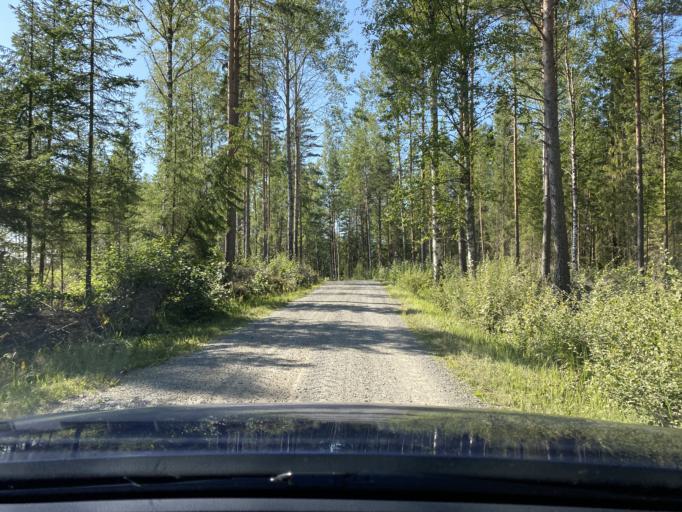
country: FI
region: Satakunta
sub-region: Rauma
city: Kiukainen
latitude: 61.1457
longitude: 22.0204
